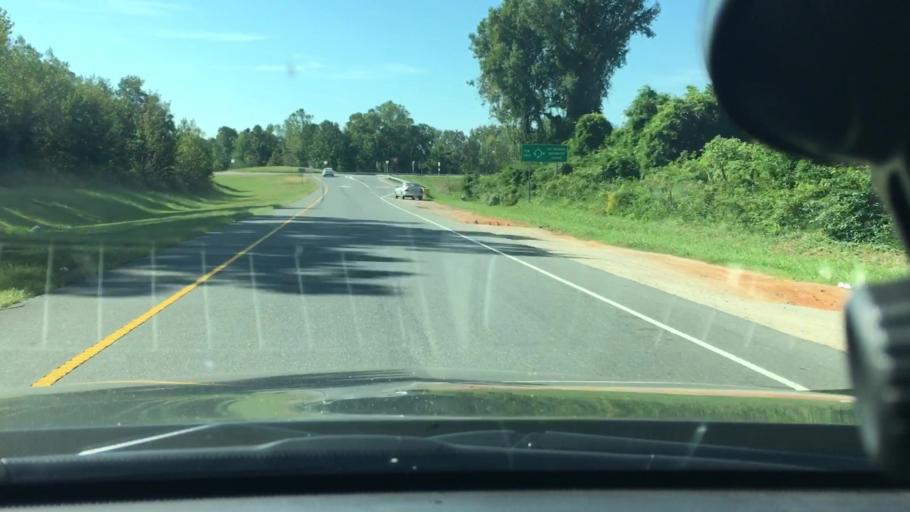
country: US
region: North Carolina
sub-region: Gaston County
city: Mount Holly
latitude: 35.2753
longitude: -80.9670
